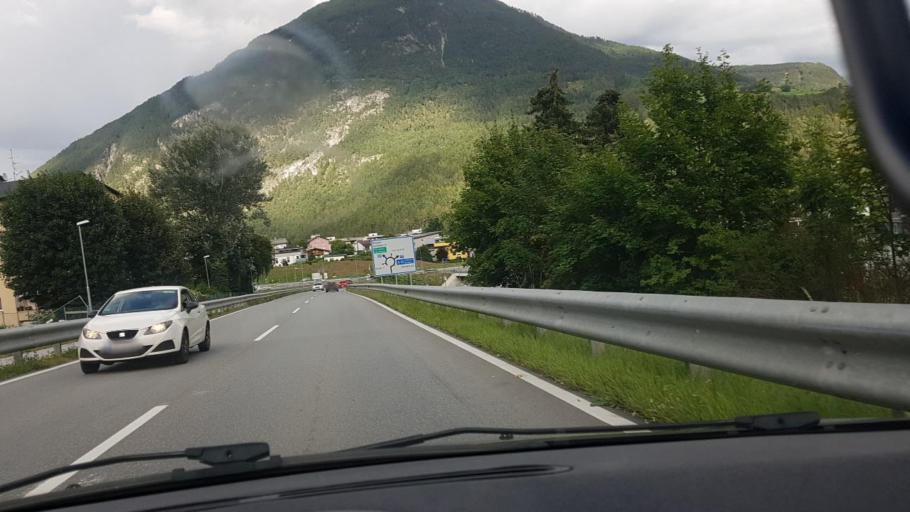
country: AT
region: Tyrol
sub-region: Politischer Bezirk Imst
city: Imst
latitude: 47.2353
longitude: 10.7406
